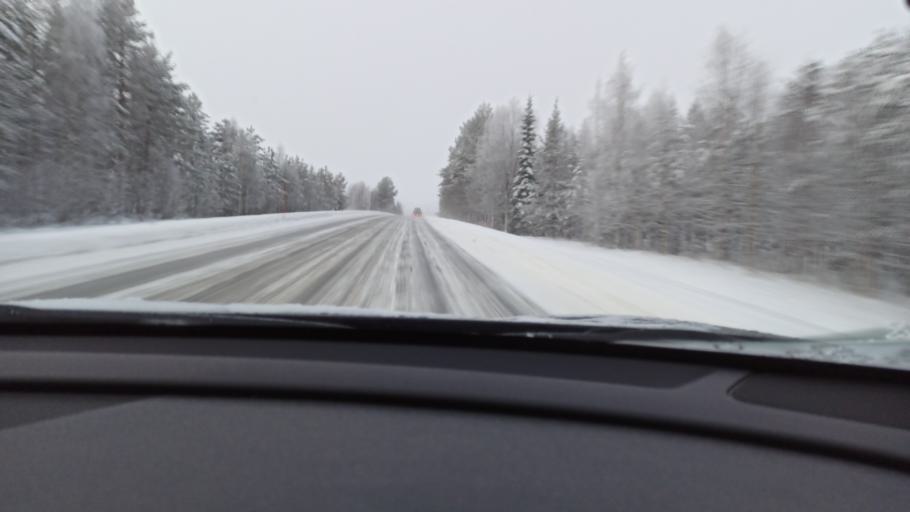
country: FI
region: Lapland
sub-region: Pohjois-Lappi
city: Sodankylae
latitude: 66.9281
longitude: 26.2285
